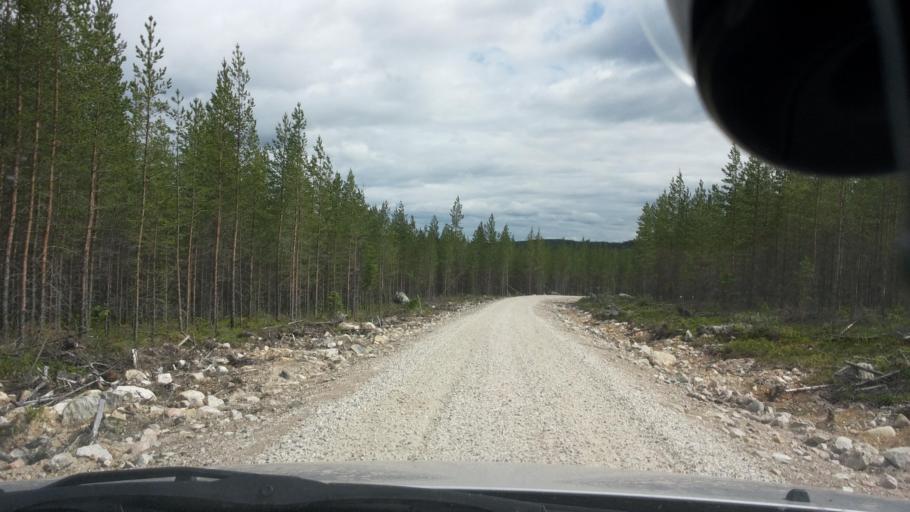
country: SE
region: Gaevleborg
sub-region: Ovanakers Kommun
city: Edsbyn
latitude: 61.4663
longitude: 15.2895
